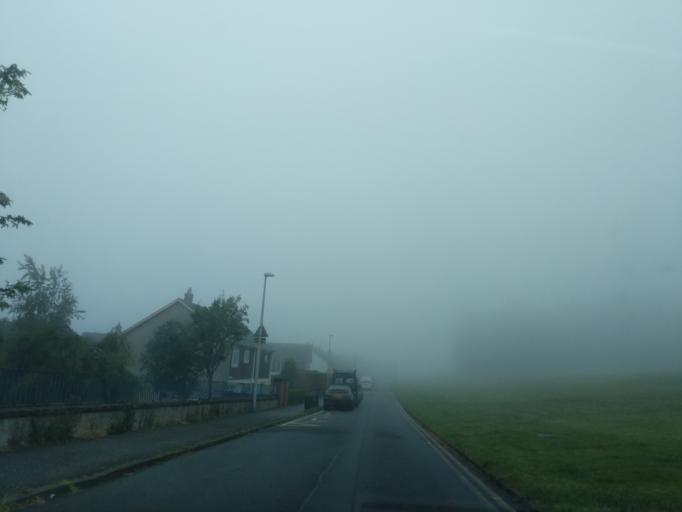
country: GB
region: Scotland
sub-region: West Lothian
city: Seafield
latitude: 55.9475
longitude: -3.1440
